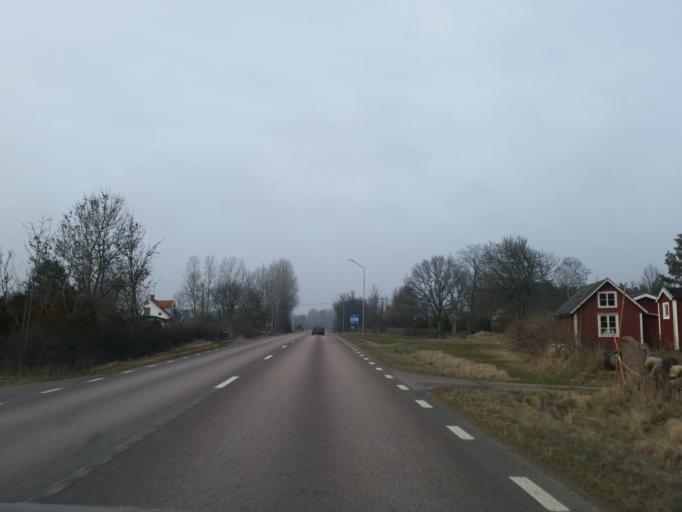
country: SE
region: Kalmar
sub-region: Borgholms Kommun
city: Borgholm
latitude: 57.1533
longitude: 17.0096
